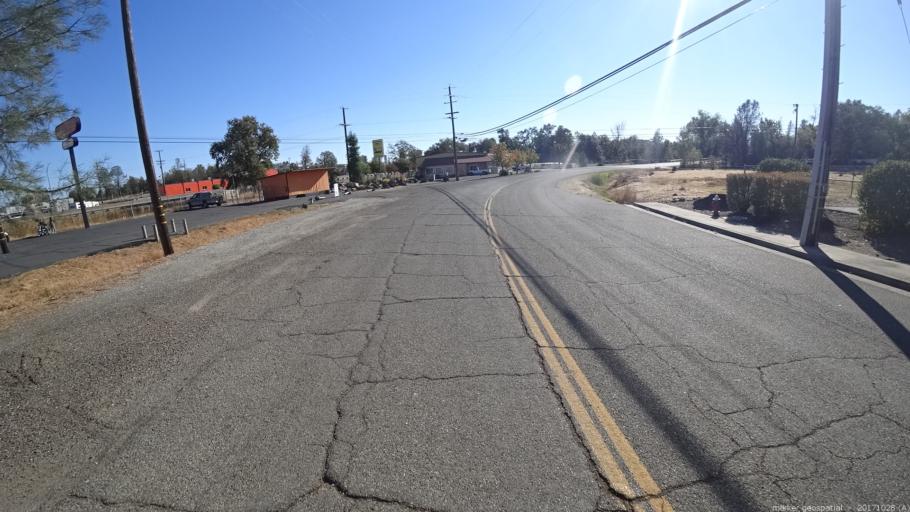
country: US
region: California
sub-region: Shasta County
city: Shasta Lake
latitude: 40.6393
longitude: -122.3668
